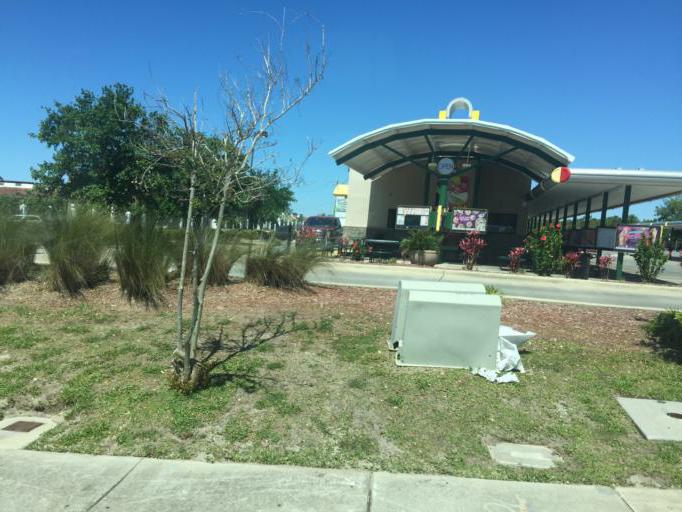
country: US
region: Florida
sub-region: Bay County
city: Panama City Beach
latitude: 30.1888
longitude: -85.8164
